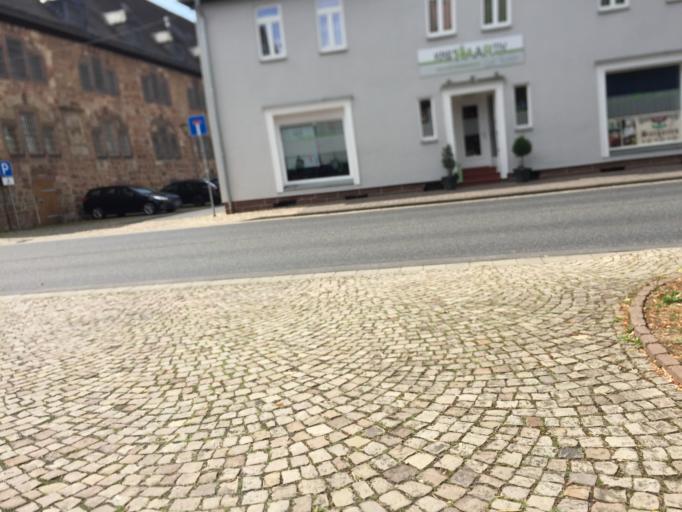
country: DE
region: Hesse
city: Schwalmstadt
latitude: 50.9102
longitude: 9.2348
